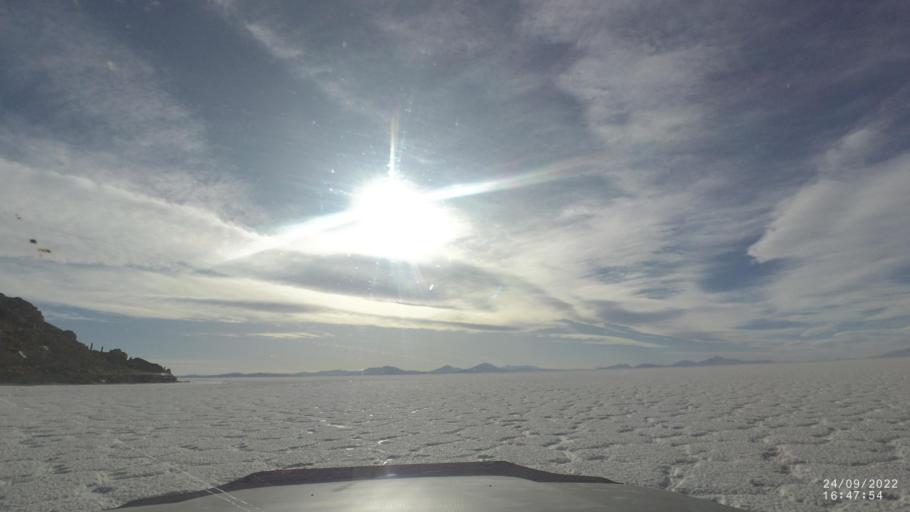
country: BO
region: Potosi
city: Colchani
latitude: -20.1315
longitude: -67.8085
